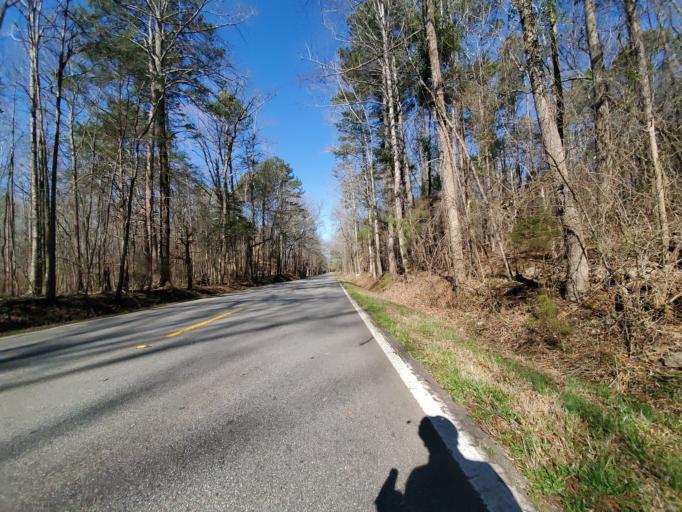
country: US
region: Georgia
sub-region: Oconee County
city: Bogart
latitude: 33.9944
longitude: -83.4895
